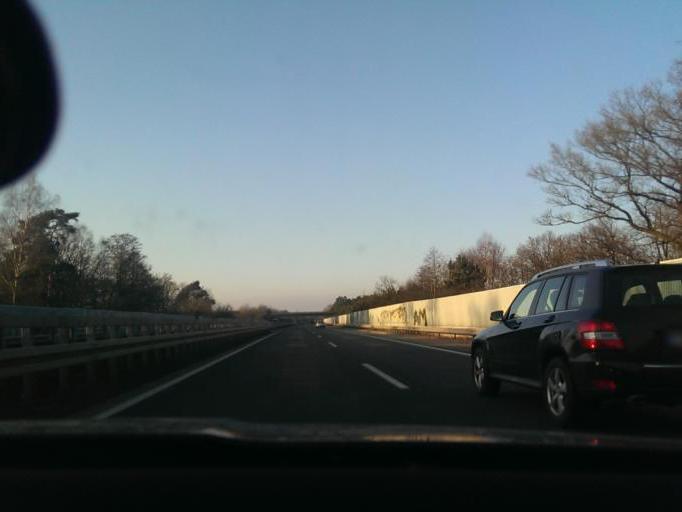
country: DE
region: North Rhine-Westphalia
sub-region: Regierungsbezirk Detmold
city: Hovelhof
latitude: 51.8674
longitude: 8.6573
